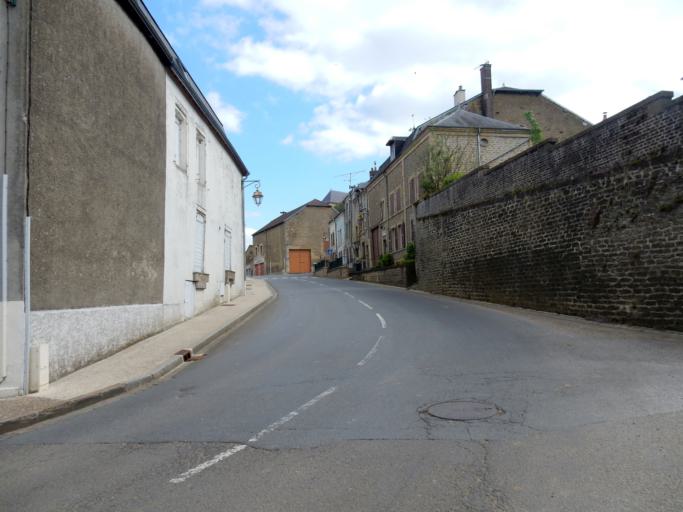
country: FR
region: Champagne-Ardenne
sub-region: Departement des Ardennes
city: Bazeilles
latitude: 49.6512
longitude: 4.9928
